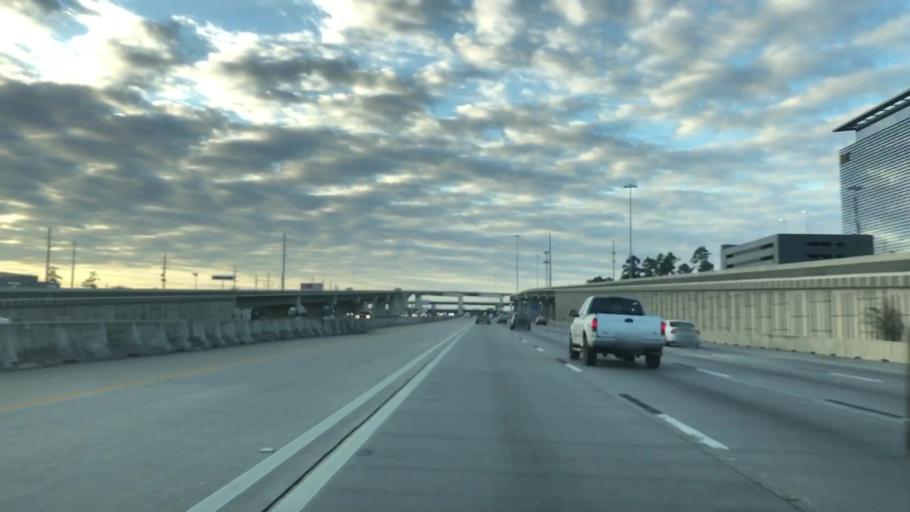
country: US
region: Texas
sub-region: Harris County
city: Spring
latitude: 30.1001
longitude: -95.4356
